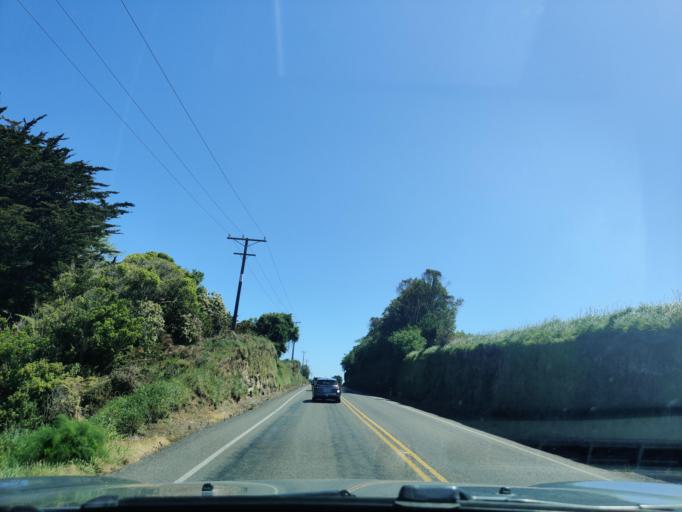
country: NZ
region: Taranaki
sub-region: South Taranaki District
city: Hawera
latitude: -39.6004
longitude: 174.3040
